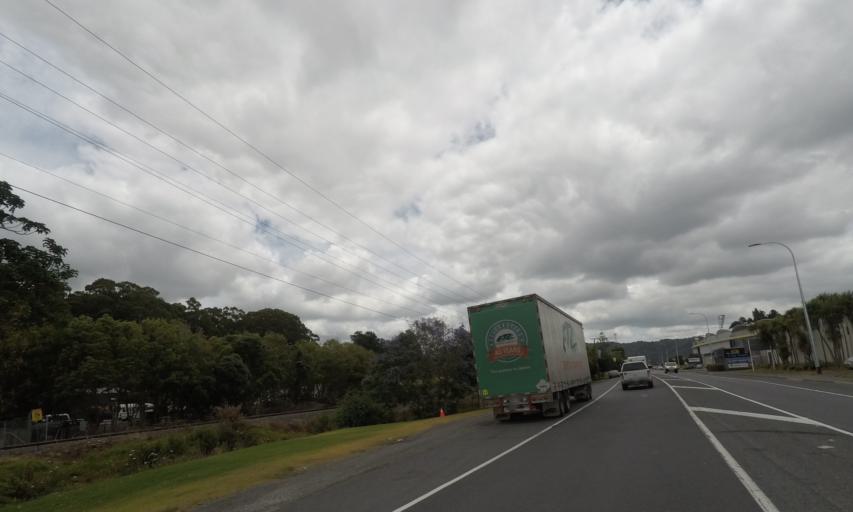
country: NZ
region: Northland
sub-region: Whangarei
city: Whangarei
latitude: -35.7363
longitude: 174.3311
